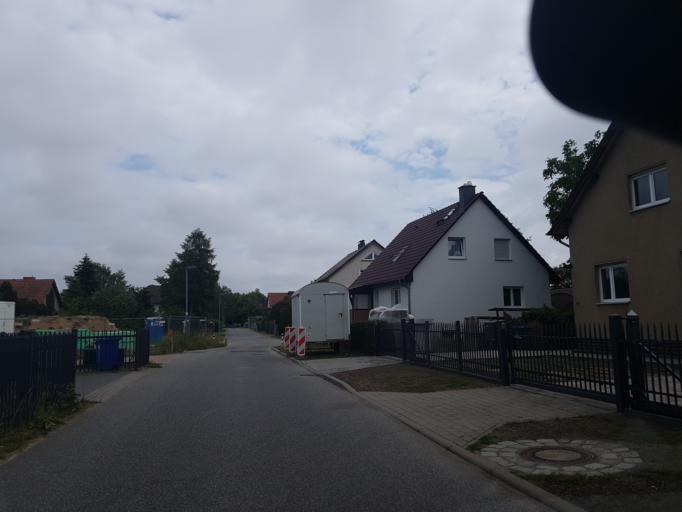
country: DE
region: Brandenburg
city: Teltow
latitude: 52.3732
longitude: 13.2570
